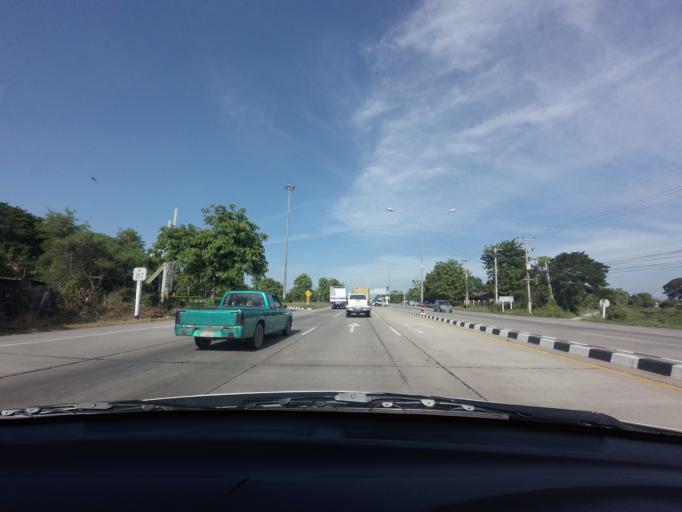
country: TH
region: Suphan Buri
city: Suphan Buri
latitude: 14.4483
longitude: 100.1109
